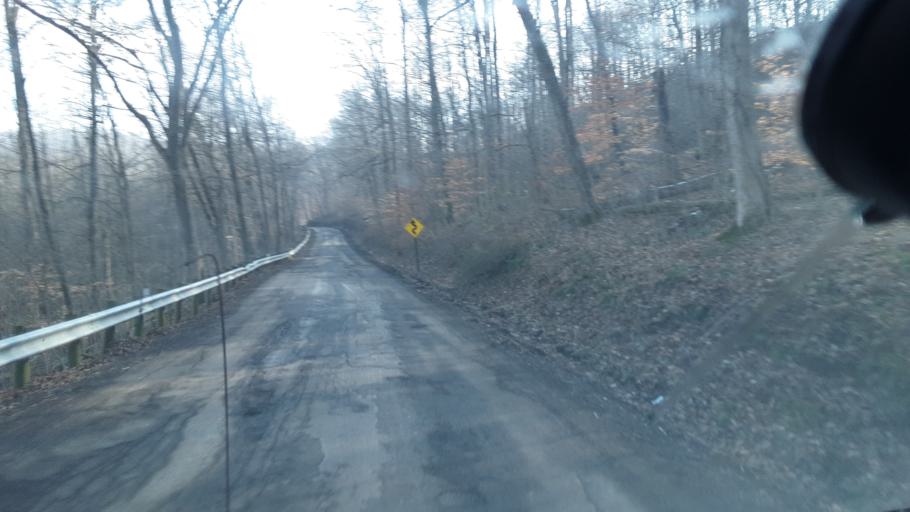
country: US
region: Ohio
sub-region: Knox County
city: Oak Hill
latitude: 40.4253
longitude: -82.1983
